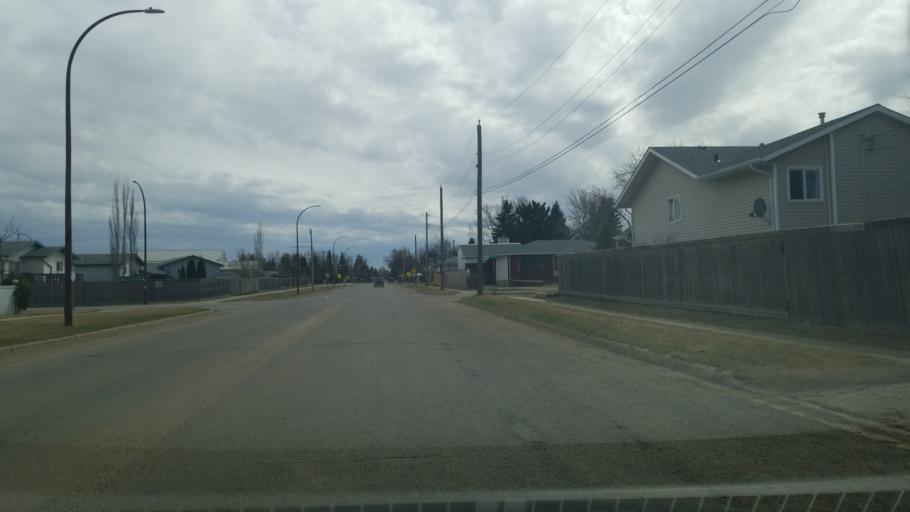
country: CA
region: Saskatchewan
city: Lloydminster
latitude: 53.2738
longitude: -109.9975
